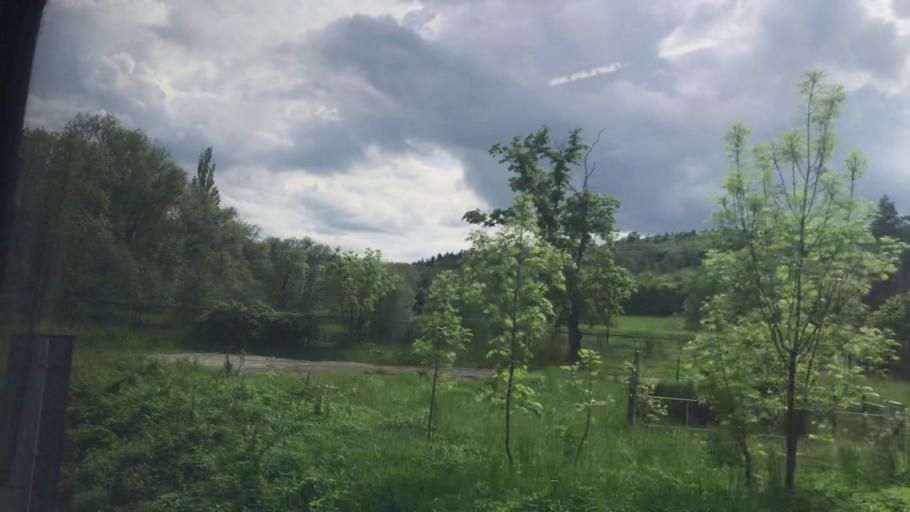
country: PL
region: Lower Silesian Voivodeship
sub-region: Powiat swidnicki
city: Swiebodzice
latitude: 50.8501
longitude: 16.3351
